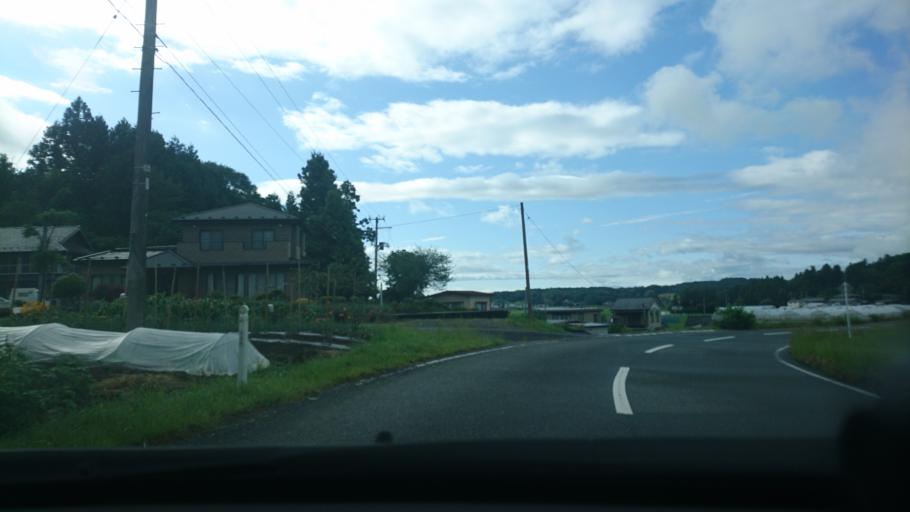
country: JP
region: Miyagi
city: Wakuya
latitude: 38.6857
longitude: 141.2836
